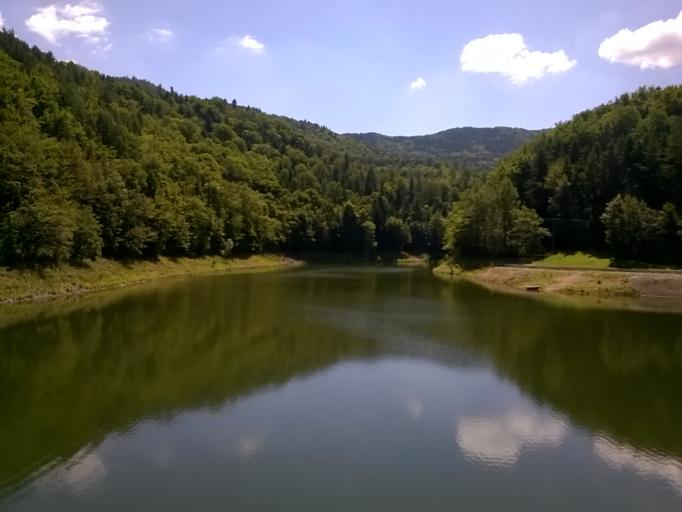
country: SK
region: Banskobystricky
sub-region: Okres Banska Bystrica
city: Banska Stiavnica
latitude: 48.4647
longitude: 18.8498
